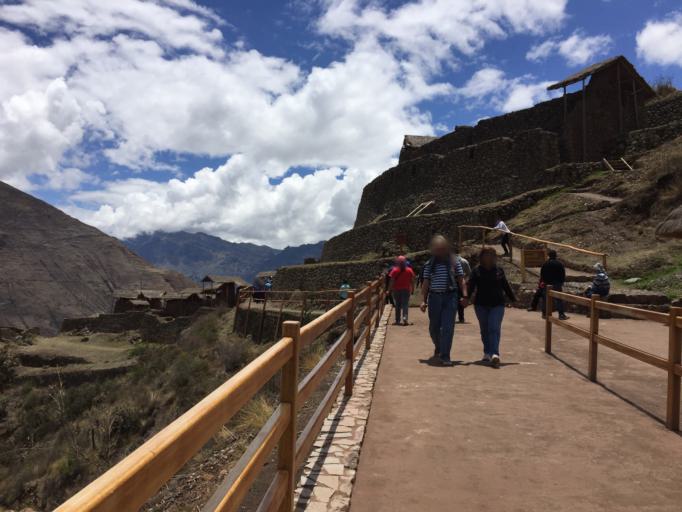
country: PE
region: Cusco
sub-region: Provincia de Calca
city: Pisac
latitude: -13.4063
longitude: -71.8415
